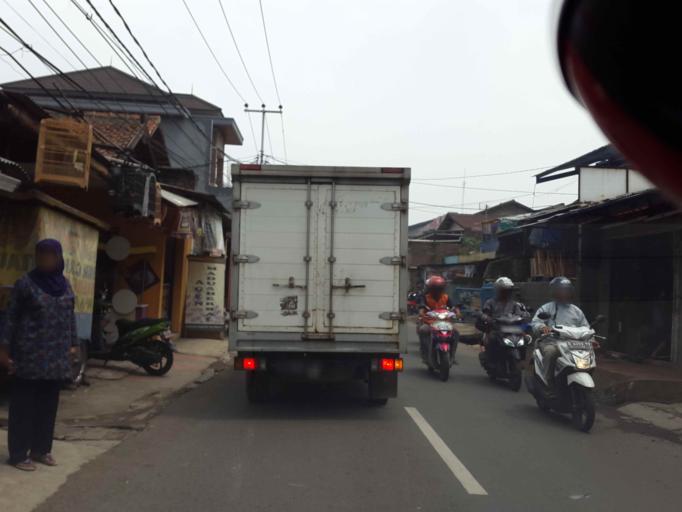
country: ID
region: West Java
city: Cimahi
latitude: -6.9123
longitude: 107.5602
